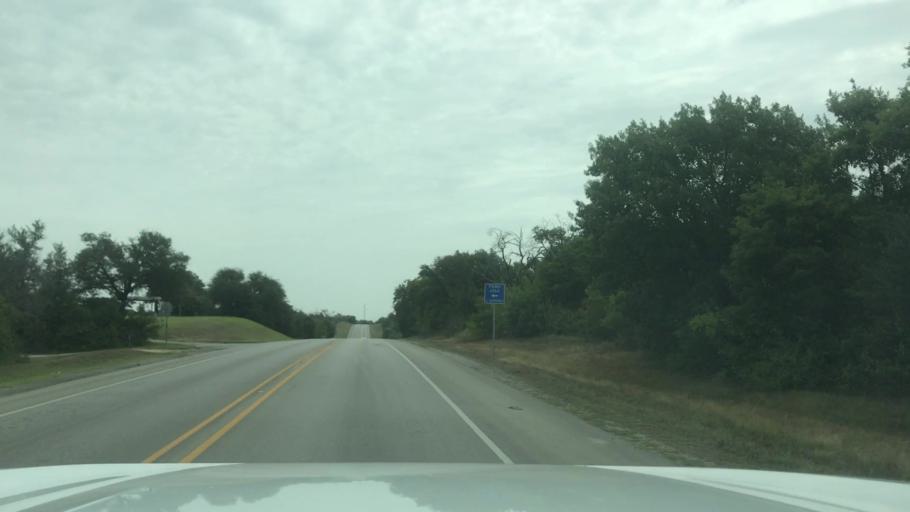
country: US
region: Texas
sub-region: Erath County
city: Dublin
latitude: 32.0981
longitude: -98.3901
